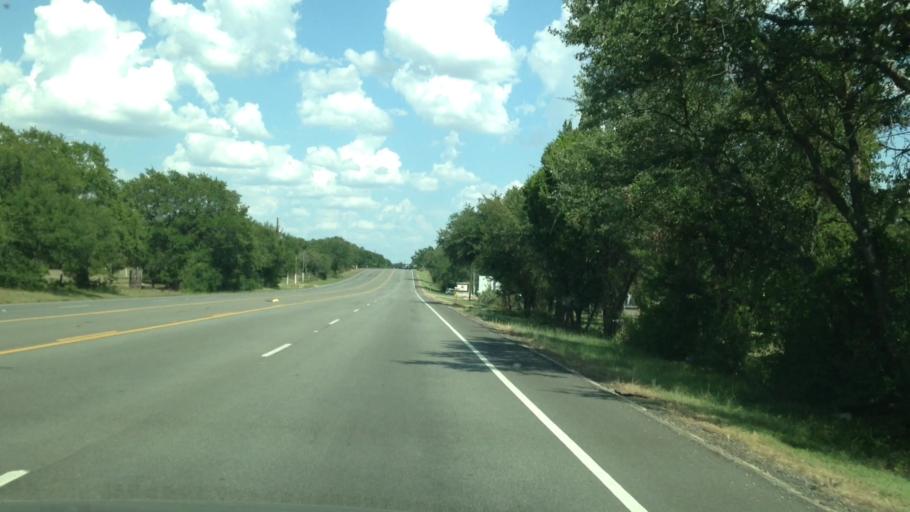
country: US
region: Texas
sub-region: Williamson County
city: Georgetown
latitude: 30.6319
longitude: -97.7576
